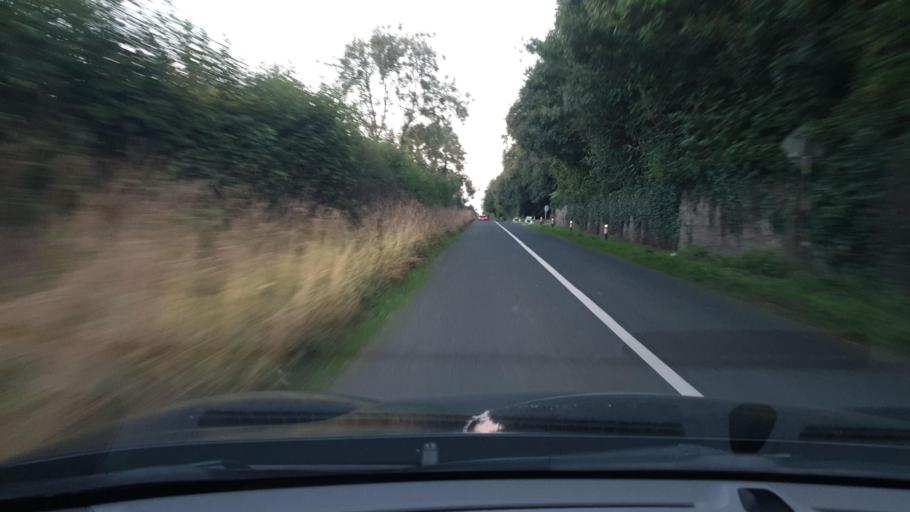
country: IE
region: Leinster
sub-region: Kildare
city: Prosperous
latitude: 53.3471
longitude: -6.7432
